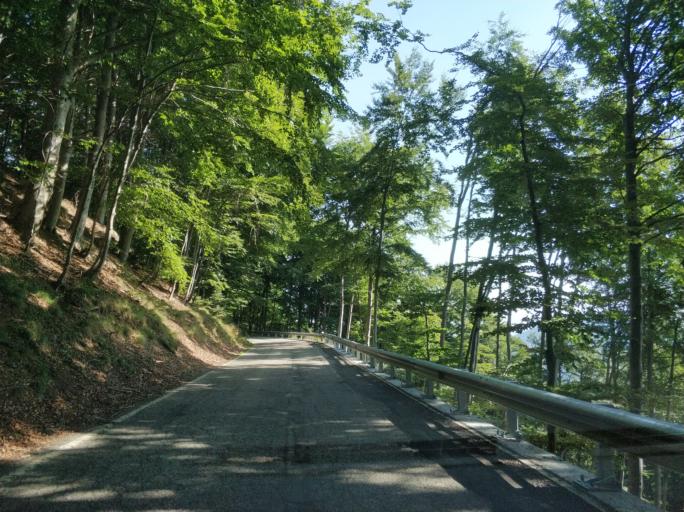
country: IT
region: Piedmont
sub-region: Provincia di Torino
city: Rubiana
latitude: 45.1845
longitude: 7.3716
